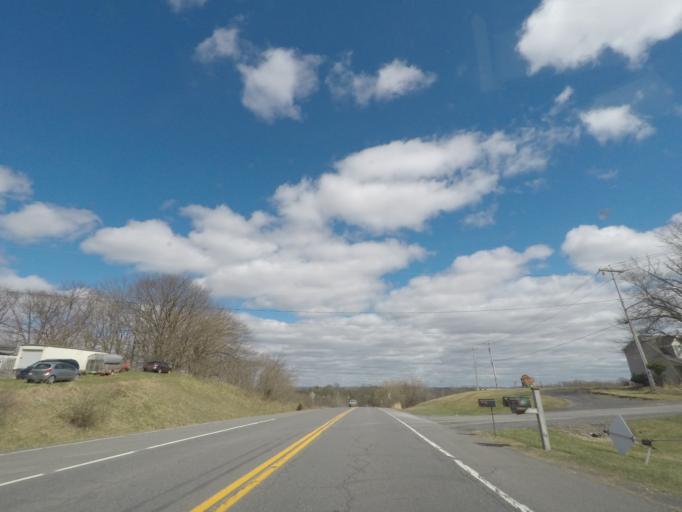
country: US
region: New York
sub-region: Albany County
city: Delmar
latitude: 42.5655
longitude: -73.8340
